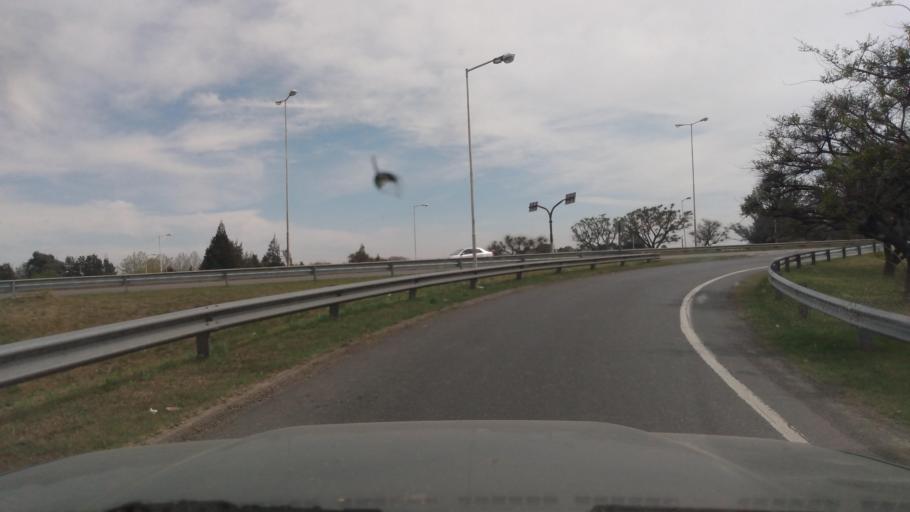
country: AR
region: Buenos Aires
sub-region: Partido de Lujan
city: Lujan
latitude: -34.5750
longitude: -59.0367
